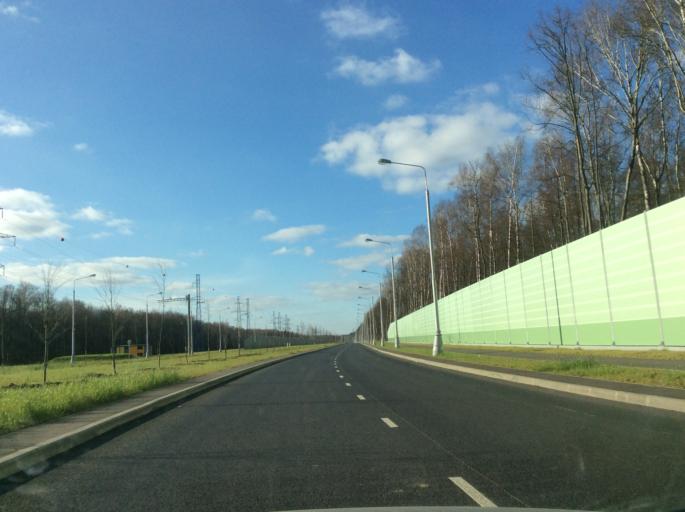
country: RU
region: Moskovskaya
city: Vatutinki
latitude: 55.4823
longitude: 37.3698
